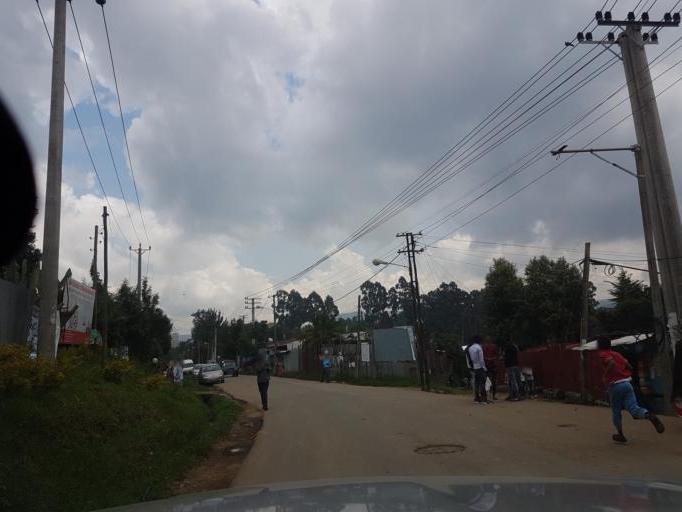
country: ET
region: Adis Abeba
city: Addis Ababa
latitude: 9.0243
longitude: 38.7680
